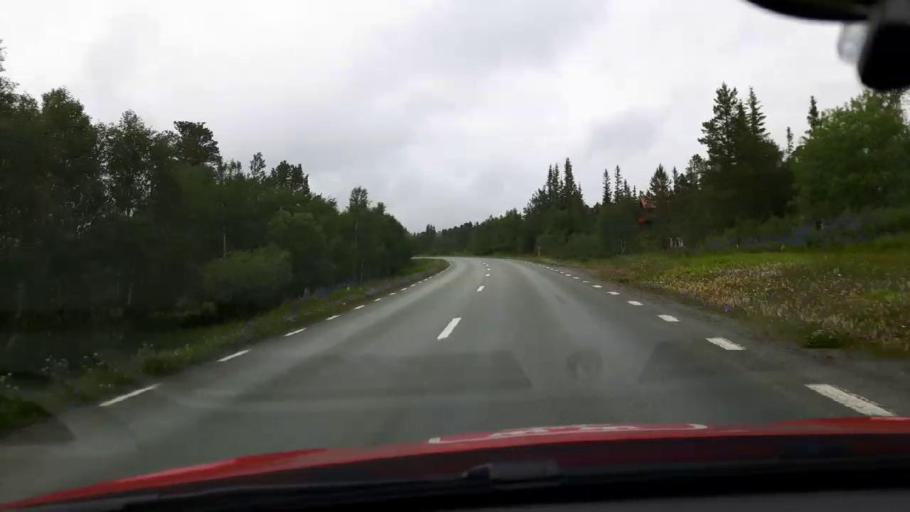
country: NO
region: Nord-Trondelag
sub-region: Meraker
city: Meraker
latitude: 63.2934
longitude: 12.1192
